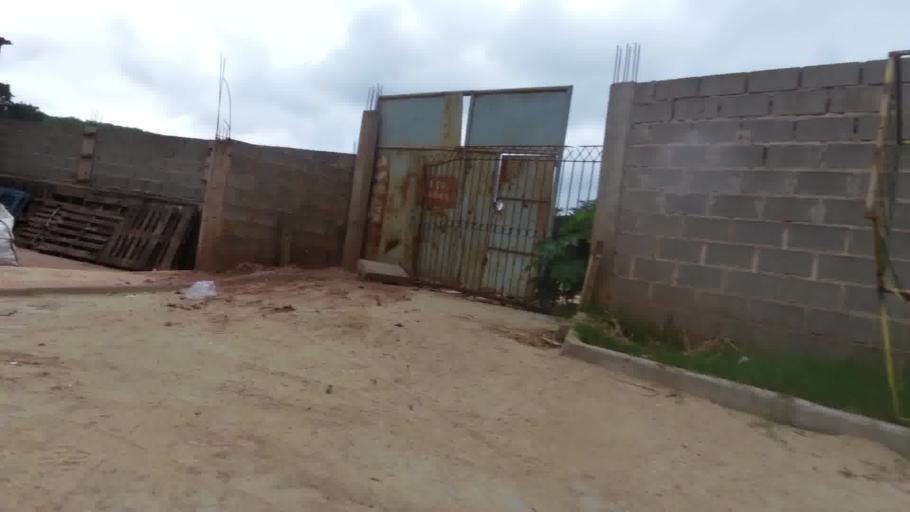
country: BR
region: Espirito Santo
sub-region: Alfredo Chaves
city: Alfredo Chaves
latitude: -20.6441
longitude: -40.7441
